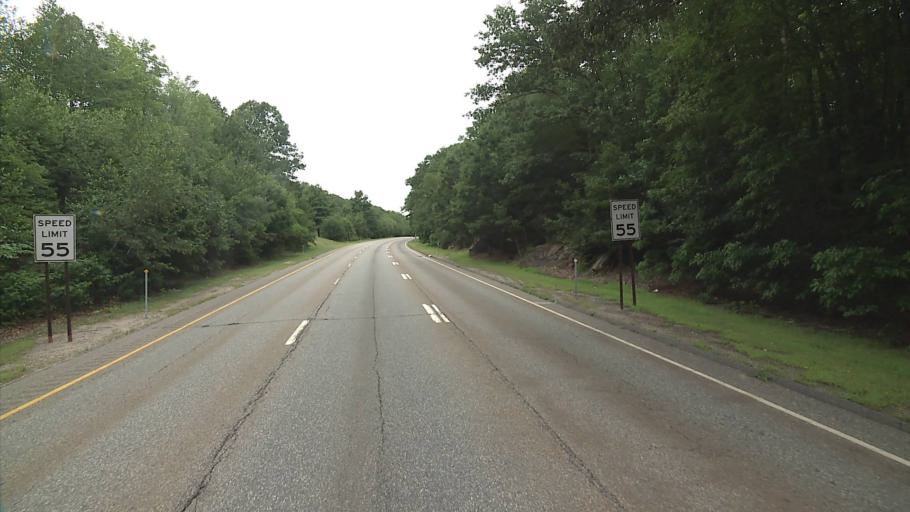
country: US
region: Connecticut
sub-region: Litchfield County
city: Thomaston
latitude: 41.7060
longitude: -73.0775
